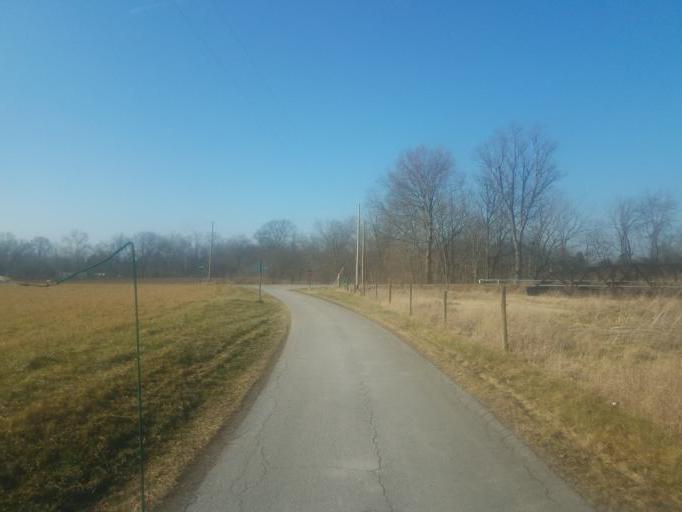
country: US
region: Ohio
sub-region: Seneca County
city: Tiffin
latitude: 41.0607
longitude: -83.0337
